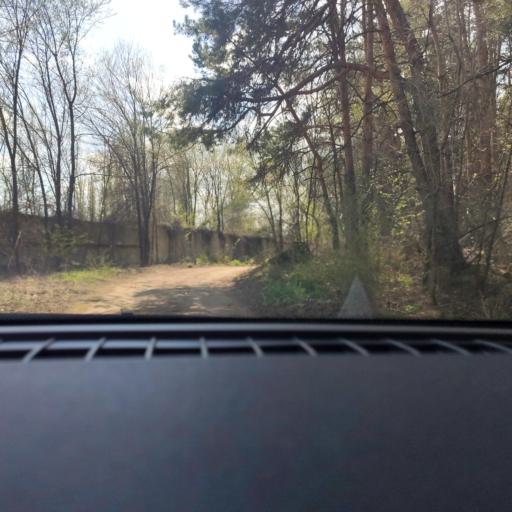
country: RU
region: Voronezj
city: Maslovka
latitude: 51.5969
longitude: 39.2193
